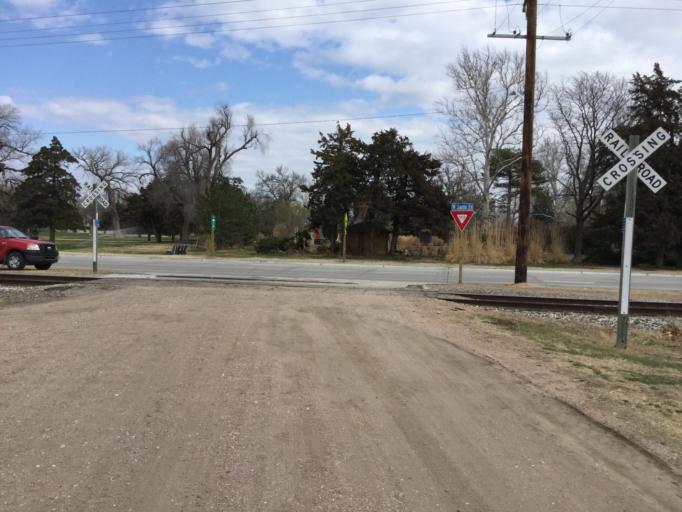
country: US
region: Kansas
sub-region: Barton County
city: Ellinwood
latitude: 38.3547
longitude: -98.5881
